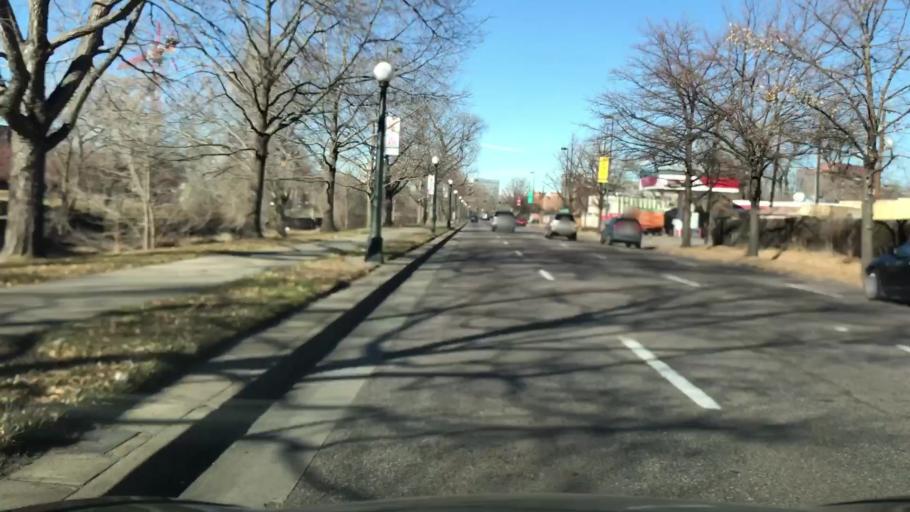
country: US
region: Colorado
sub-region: Denver County
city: Denver
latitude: 39.7217
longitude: -104.9801
